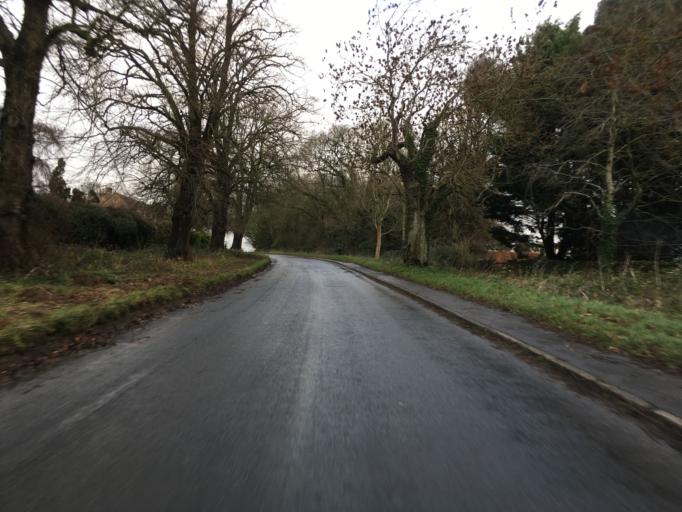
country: GB
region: England
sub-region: Gloucestershire
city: Tetbury
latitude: 51.6291
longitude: -2.1322
